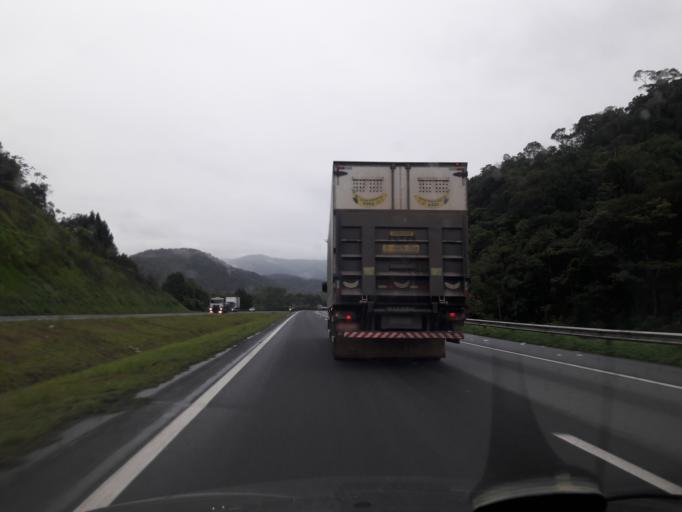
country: BR
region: Sao Paulo
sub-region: Miracatu
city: Miracatu
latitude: -24.2281
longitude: -47.3626
